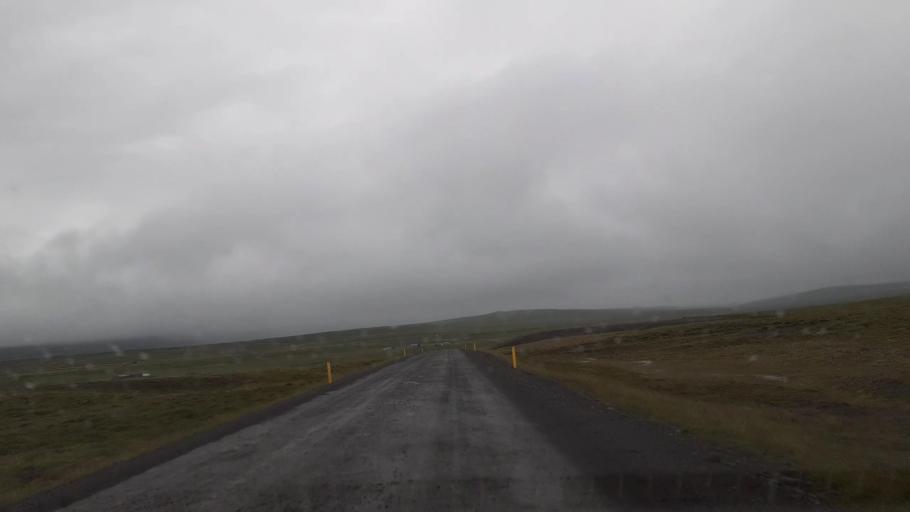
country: IS
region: East
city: Egilsstadir
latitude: 66.0482
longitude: -15.0936
